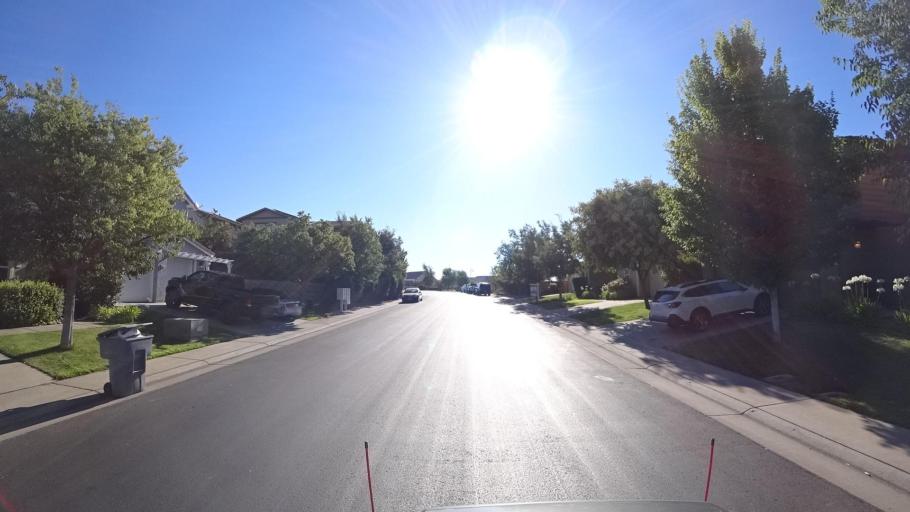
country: US
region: California
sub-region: Placer County
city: Rocklin
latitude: 38.8296
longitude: -121.2724
